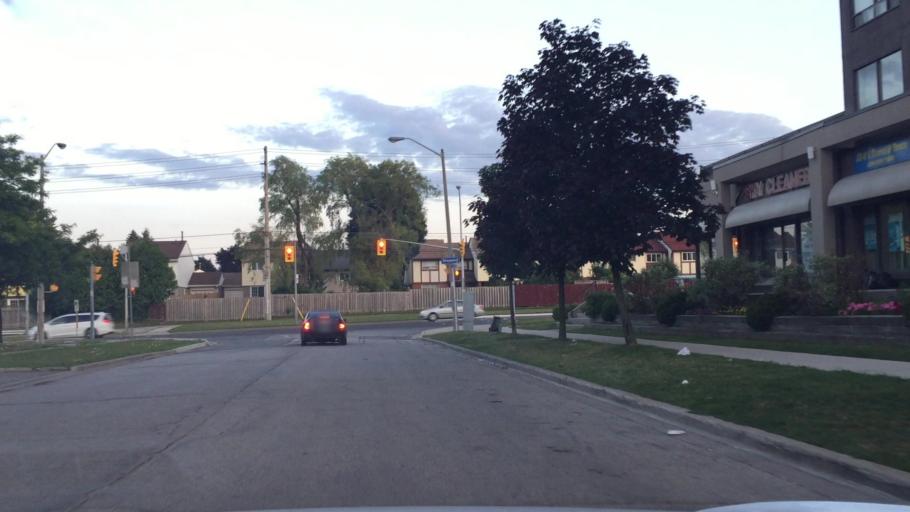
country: CA
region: Ontario
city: Scarborough
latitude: 43.7961
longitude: -79.2306
